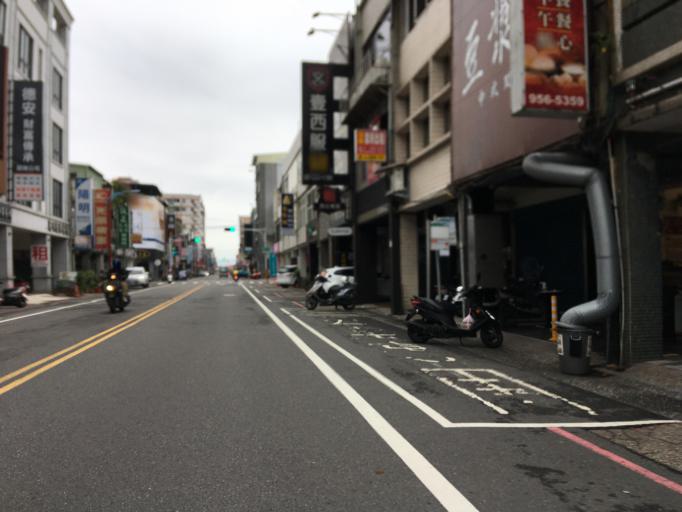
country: TW
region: Taiwan
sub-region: Yilan
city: Yilan
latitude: 24.6818
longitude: 121.7696
